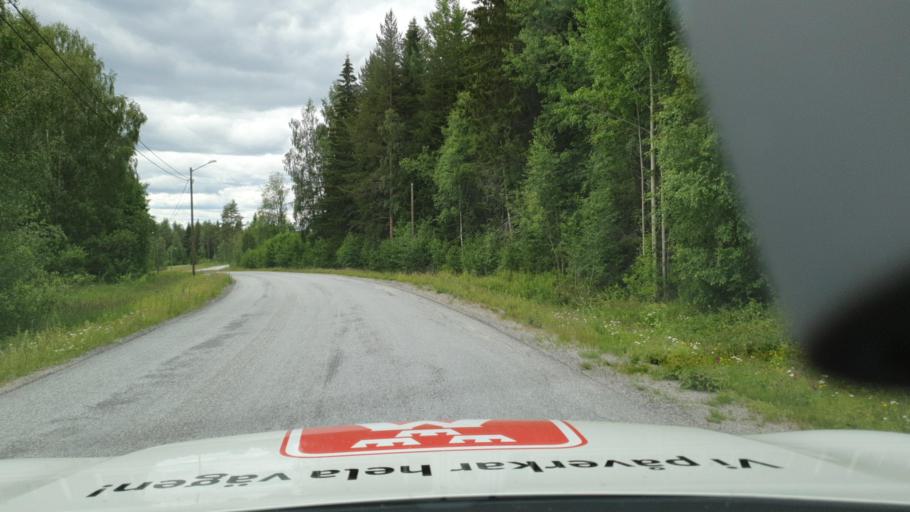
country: SE
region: Vaesterbotten
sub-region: Bjurholms Kommun
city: Bjurholm
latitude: 63.7817
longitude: 19.2191
